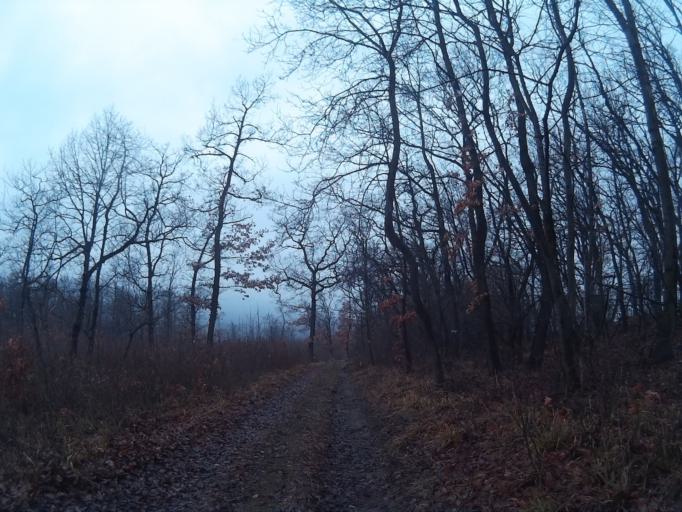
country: HU
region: Komarom-Esztergom
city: Nyergesujfalu
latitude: 47.7036
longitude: 18.5656
